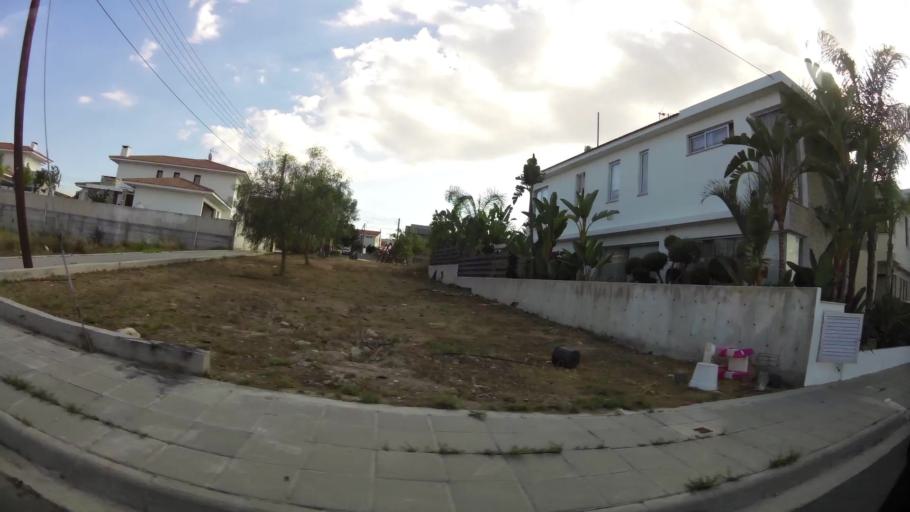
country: CY
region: Larnaka
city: Aradippou
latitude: 34.9428
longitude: 33.6083
